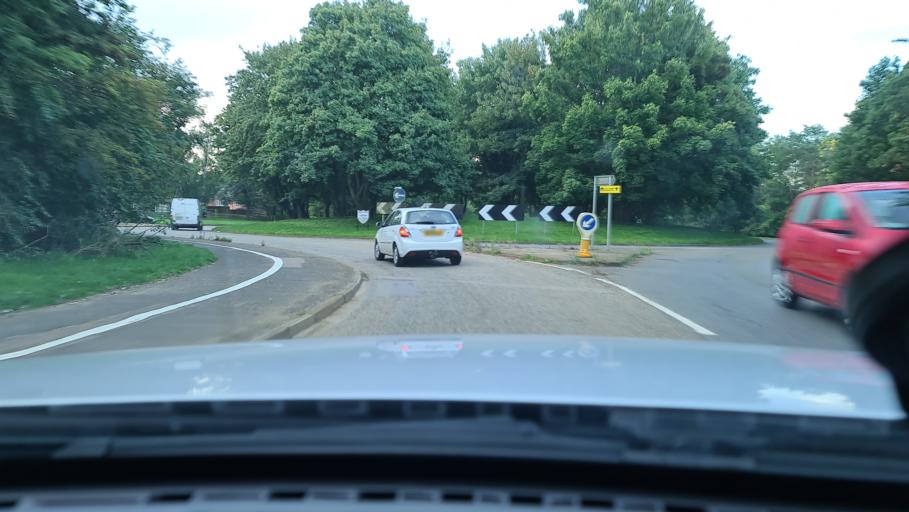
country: GB
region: England
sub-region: Oxfordshire
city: Hanwell
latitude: 52.0755
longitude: -1.3659
